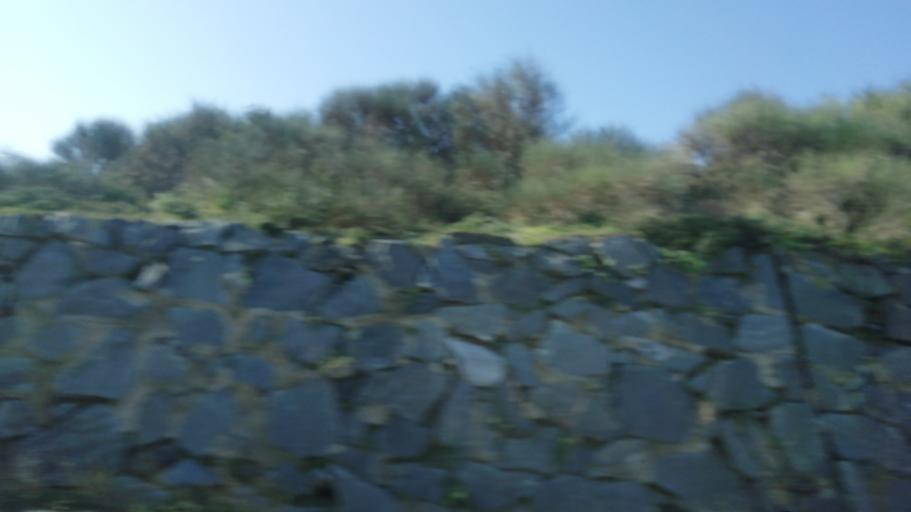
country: TR
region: Istanbul
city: Basaksehir
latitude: 41.1065
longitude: 28.7994
